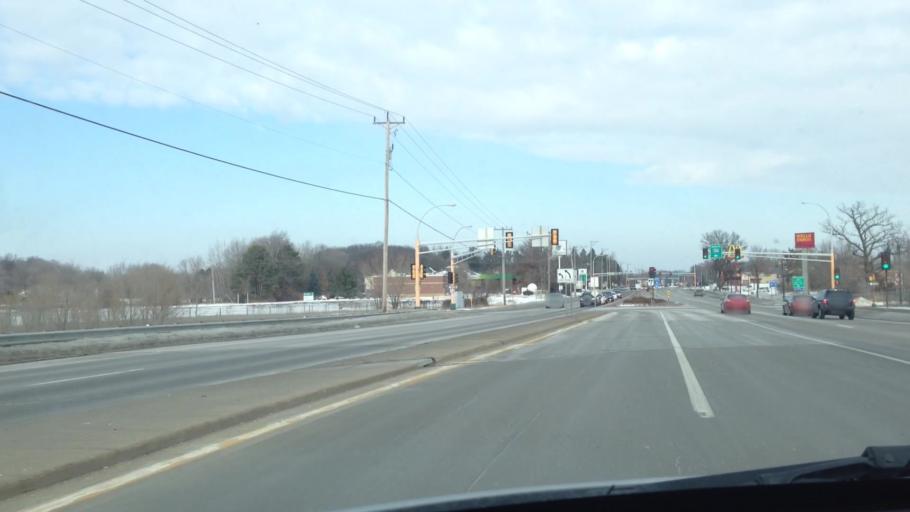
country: US
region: Minnesota
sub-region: Anoka County
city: Lino Lakes
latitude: 45.1803
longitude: -93.1128
